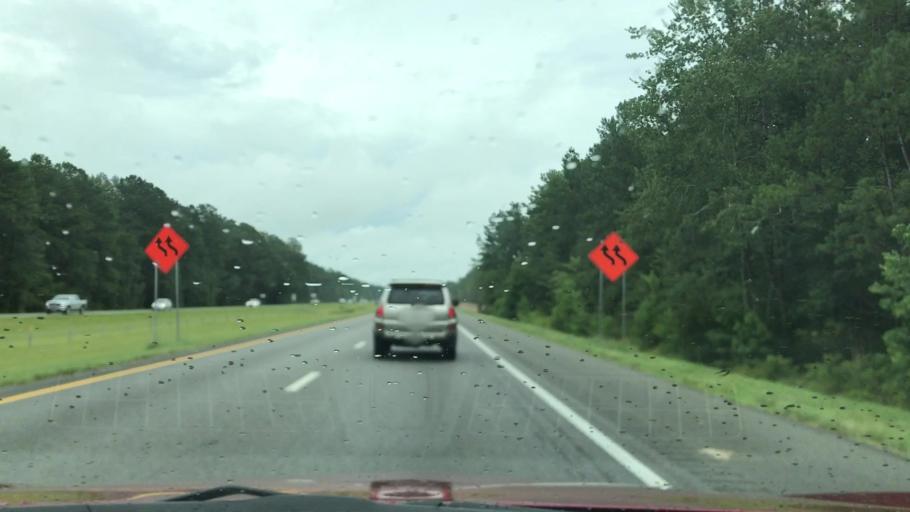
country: US
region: South Carolina
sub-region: Dorchester County
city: Ridgeville
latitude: 33.1268
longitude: -80.2894
